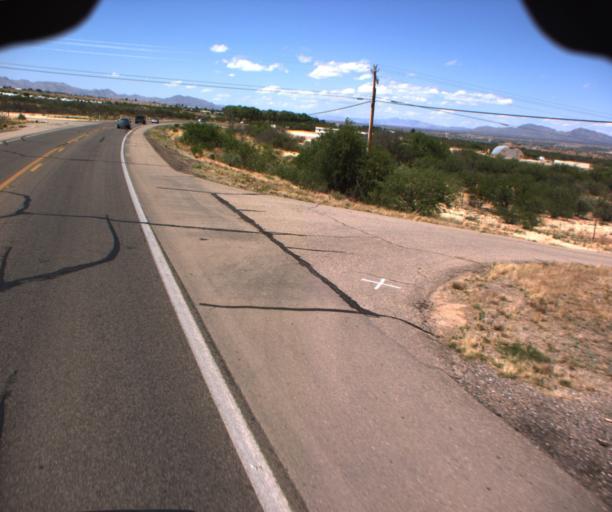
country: US
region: Arizona
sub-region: Cochise County
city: Benson
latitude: 31.9338
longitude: -110.2849
